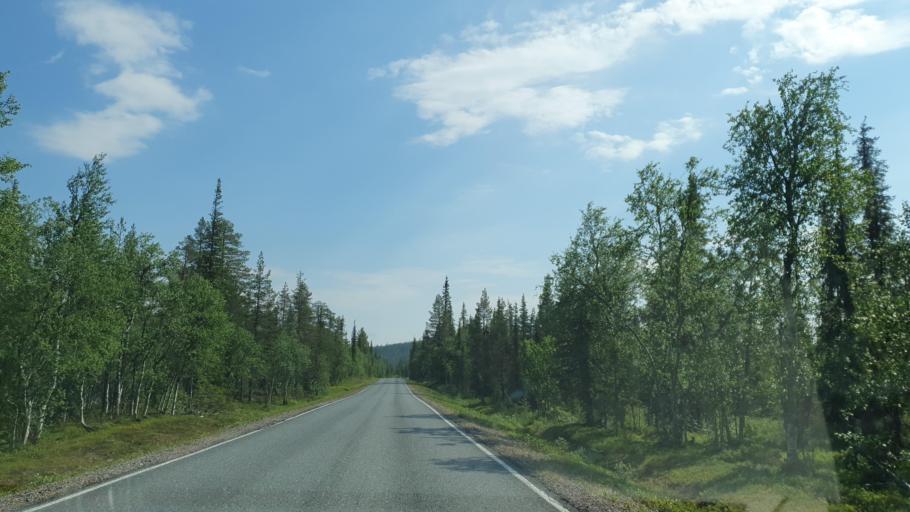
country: FI
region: Lapland
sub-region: Tunturi-Lappi
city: Muonio
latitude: 68.0164
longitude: 24.0890
